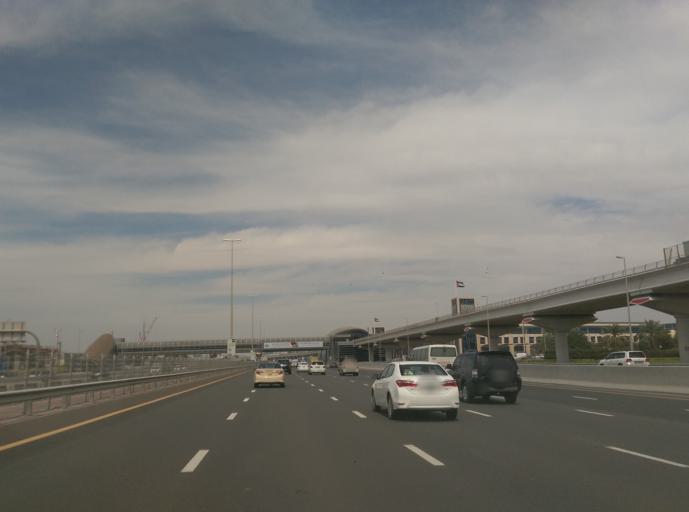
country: AE
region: Dubai
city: Dubai
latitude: 25.1249
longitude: 55.2047
